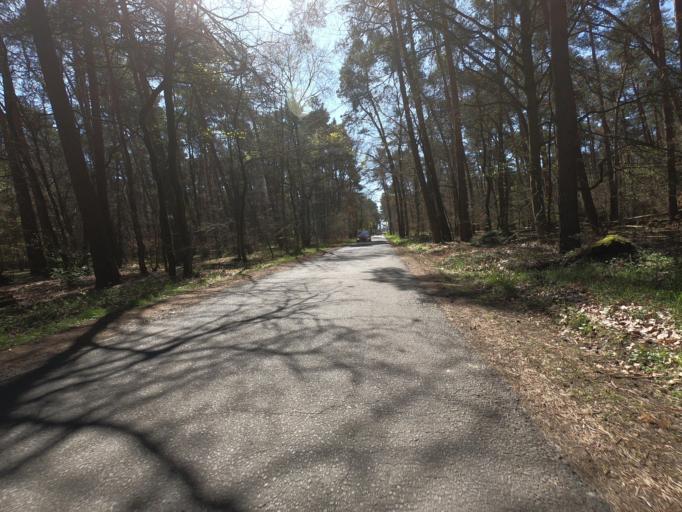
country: DE
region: Hesse
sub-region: Regierungsbezirk Darmstadt
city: Erzhausen
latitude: 49.9406
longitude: 8.6148
